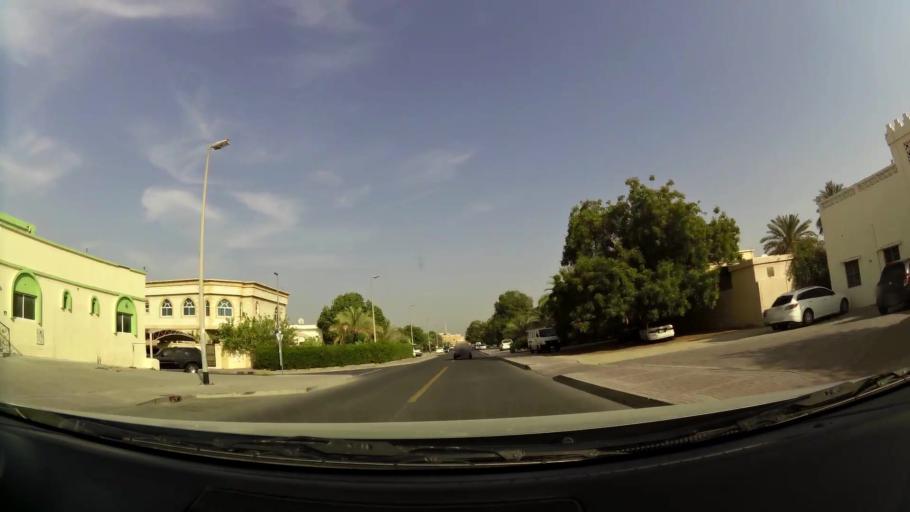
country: AE
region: Ash Shariqah
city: Sharjah
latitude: 25.2238
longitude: 55.3815
